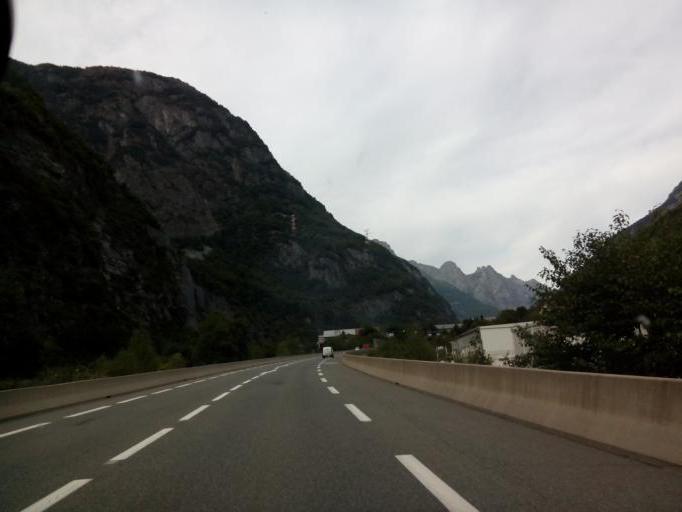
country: FR
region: Rhone-Alpes
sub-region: Departement de l'Isere
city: Vaulnaveys-le-Bas
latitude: 45.0692
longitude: 5.8701
